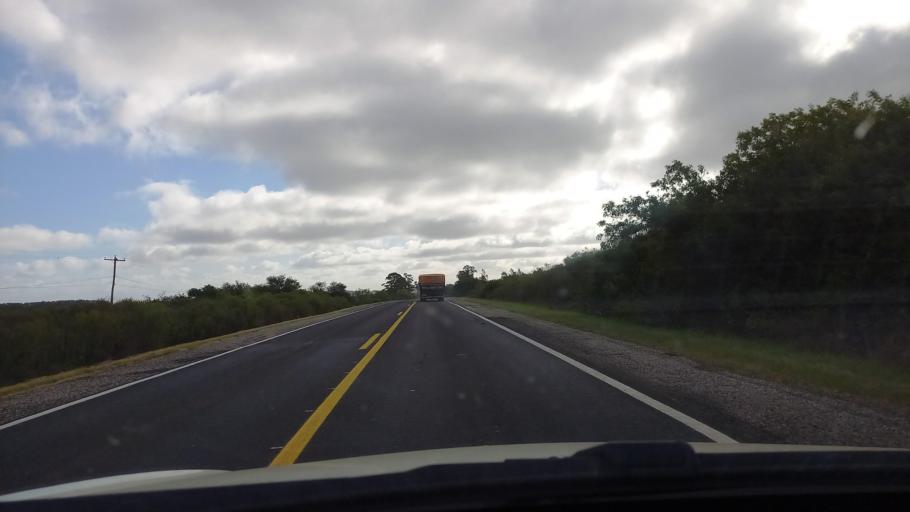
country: BR
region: Rio Grande do Sul
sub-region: Dom Pedrito
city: Dom Pedrito
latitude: -30.8995
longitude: -54.8385
